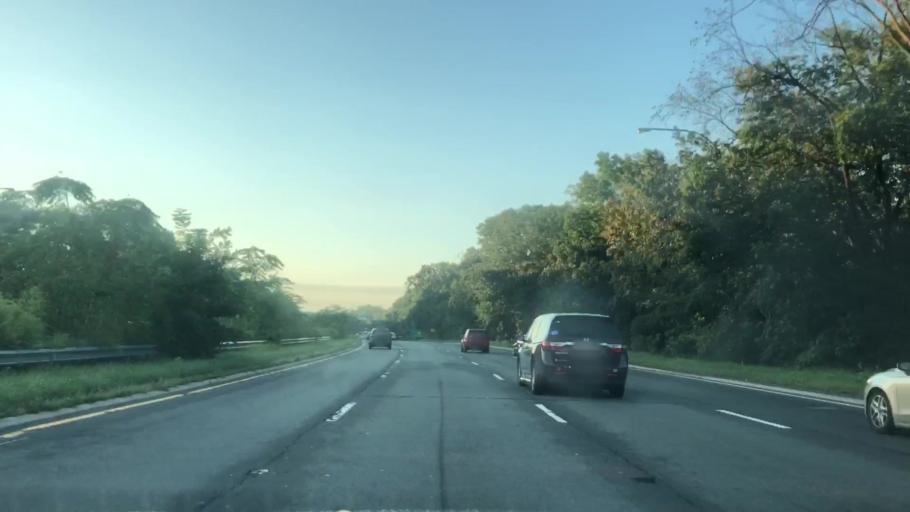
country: US
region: New York
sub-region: Nassau County
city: East Williston
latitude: 40.7628
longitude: -73.6249
